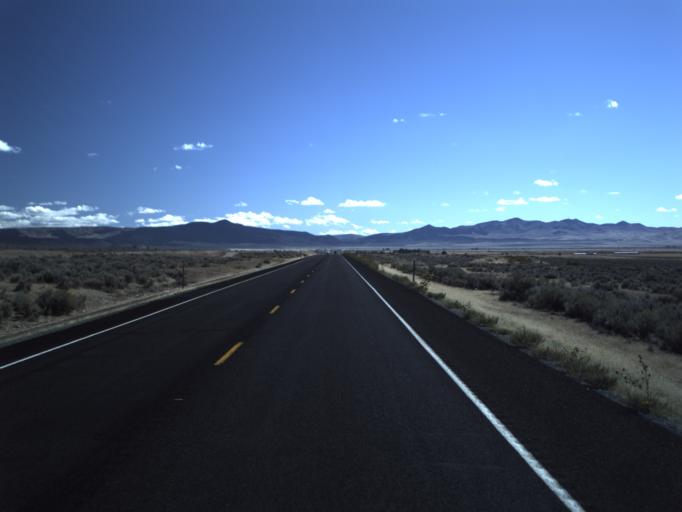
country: US
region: Utah
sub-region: Beaver County
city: Milford
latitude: 38.2994
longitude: -112.9688
